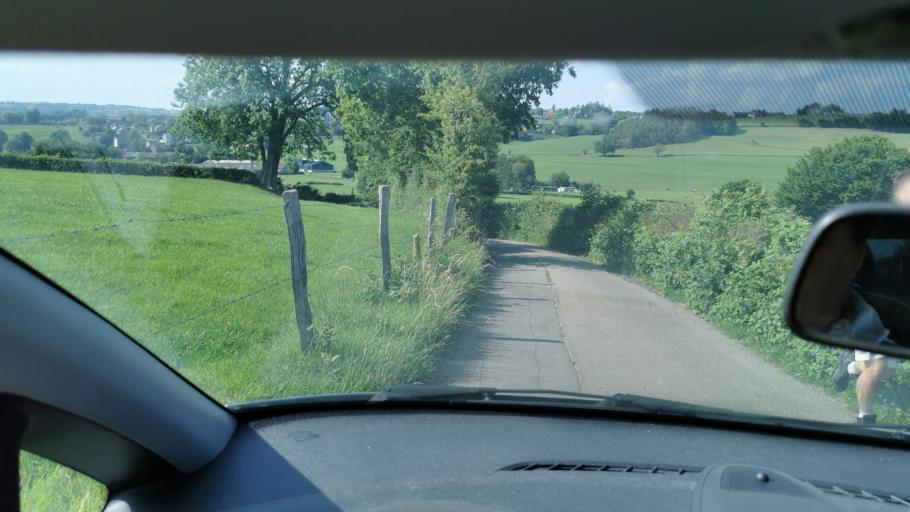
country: BE
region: Wallonia
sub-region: Province de Liege
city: Theux
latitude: 50.5391
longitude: 5.8384
